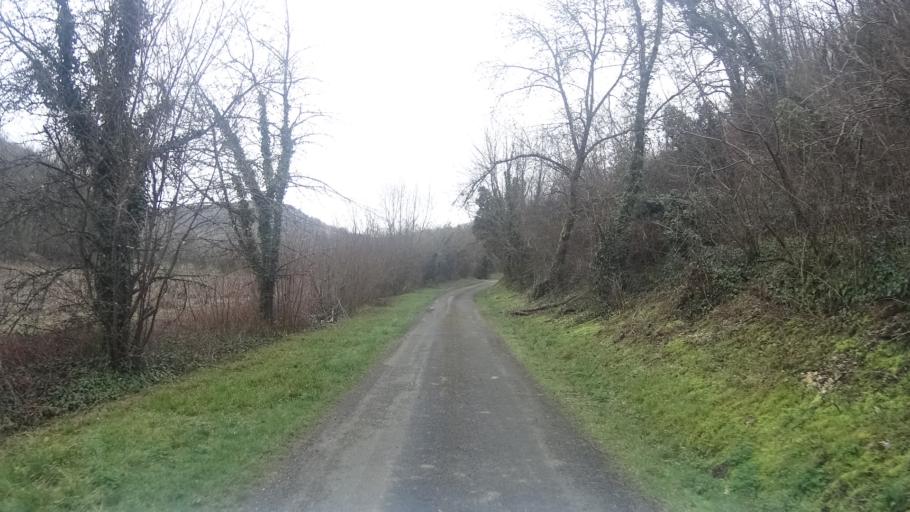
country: FR
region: Aquitaine
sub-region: Departement de la Dordogne
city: Terrasson-Lavilledieu
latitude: 45.1080
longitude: 1.2405
